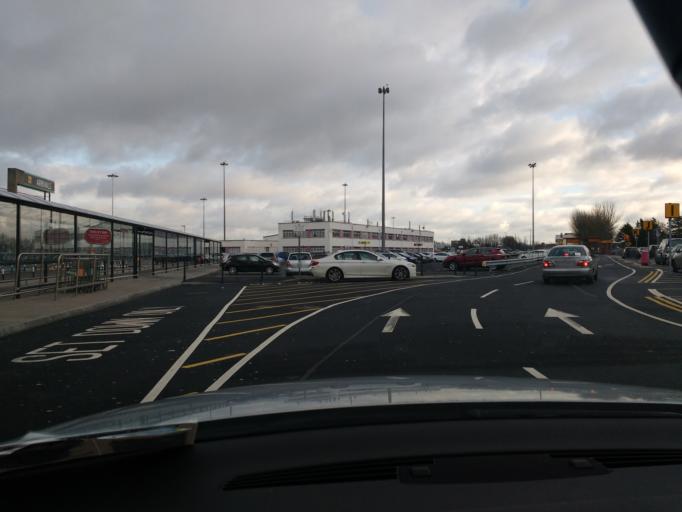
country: IE
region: Munster
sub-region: An Clar
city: Shannon
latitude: 52.6921
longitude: -8.9212
